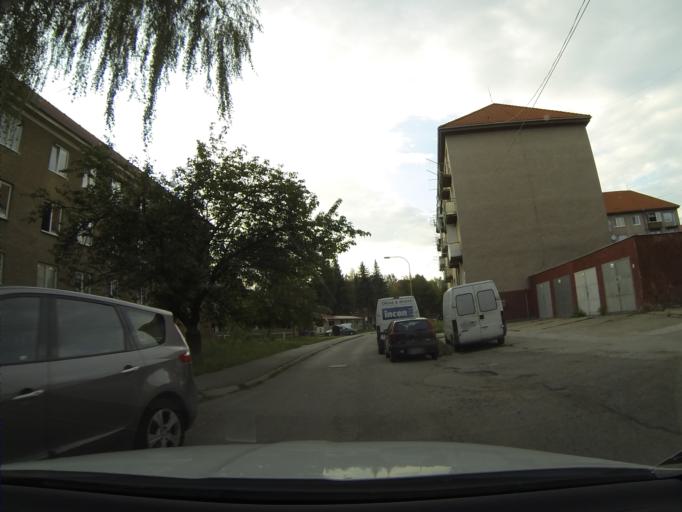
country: SK
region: Nitriansky
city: Bojnice
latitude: 48.7687
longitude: 18.5990
